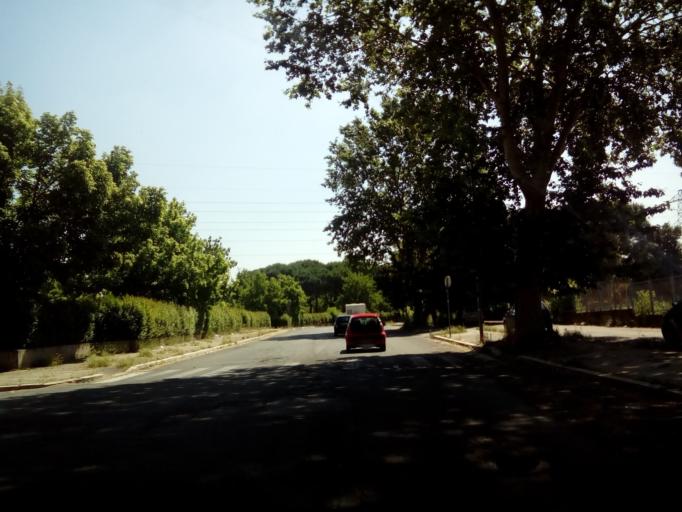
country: IT
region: Latium
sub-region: Citta metropolitana di Roma Capitale
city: Rome
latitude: 41.8900
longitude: 12.5781
